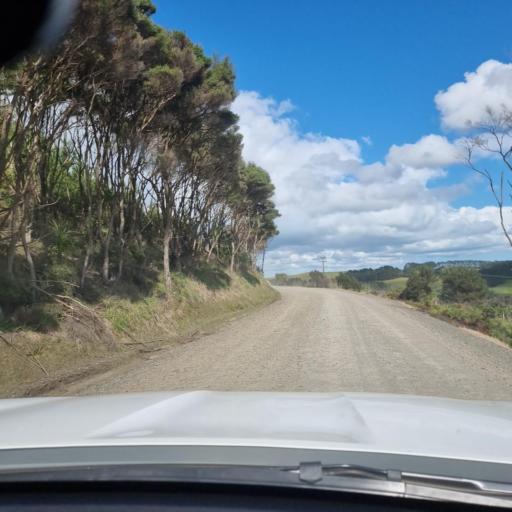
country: NZ
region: Auckland
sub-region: Auckland
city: Wellsford
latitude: -36.3234
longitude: 174.1380
